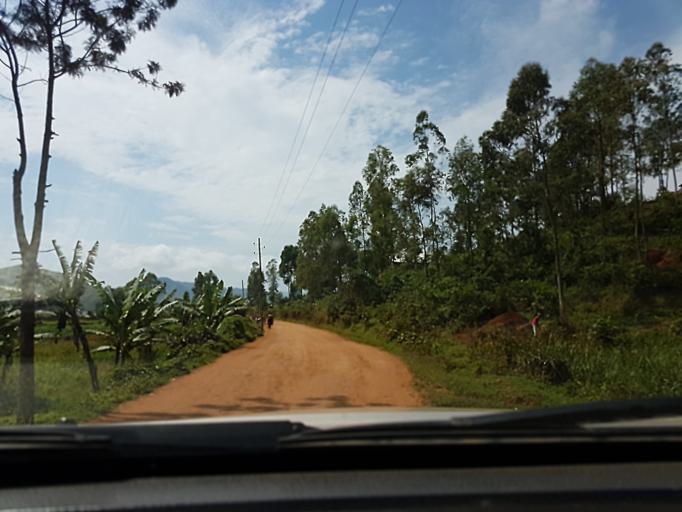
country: CD
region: South Kivu
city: Bukavu
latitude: -2.6541
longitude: 28.8738
